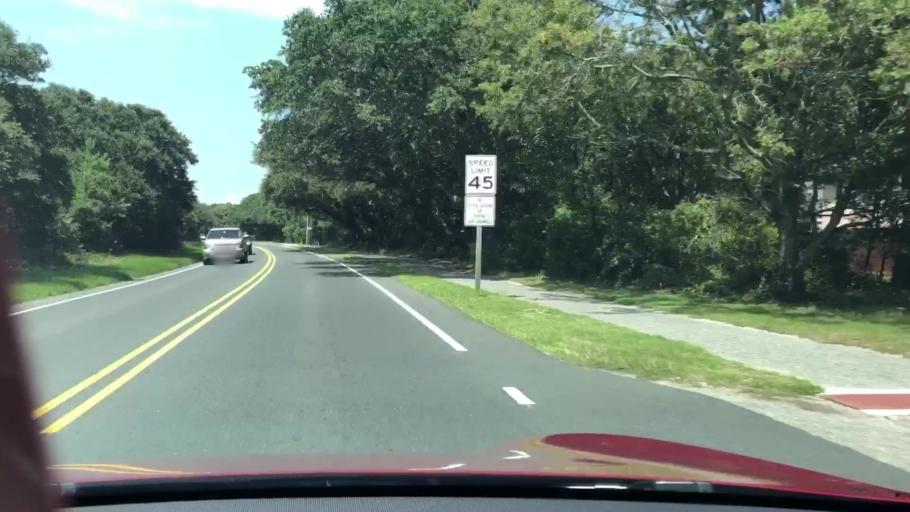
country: US
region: North Carolina
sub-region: Dare County
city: Southern Shores
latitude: 36.1395
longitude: -75.7367
